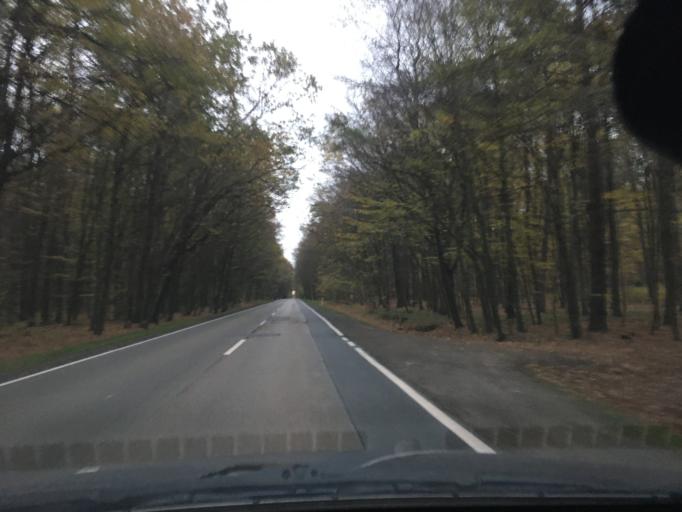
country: PL
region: Masovian Voivodeship
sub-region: Powiat pruszkowski
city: Nadarzyn
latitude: 52.1001
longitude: 20.8537
